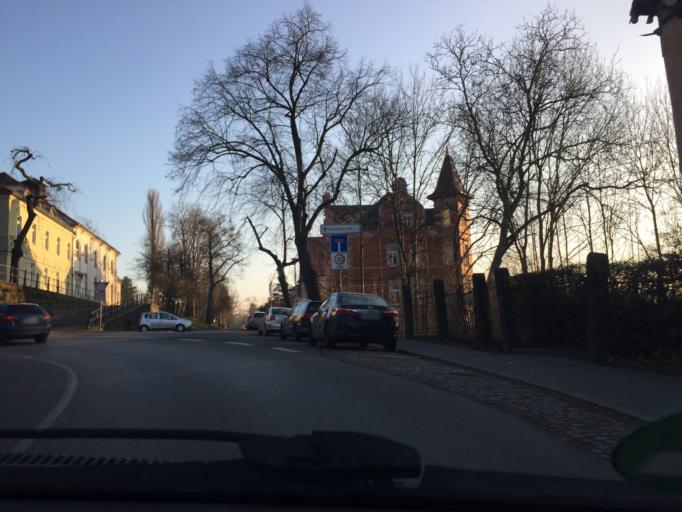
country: DE
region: Saxony
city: Pirna
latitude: 50.9562
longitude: 13.9444
